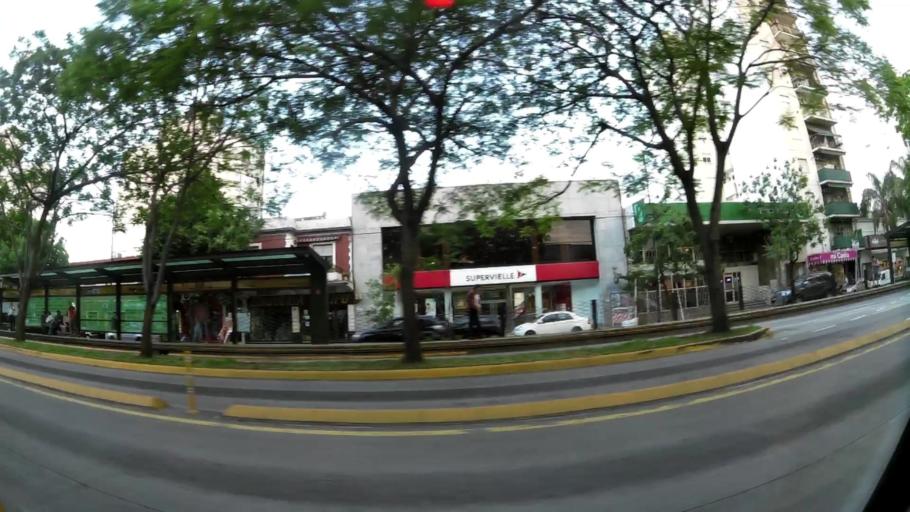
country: AR
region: Buenos Aires
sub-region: Partido de Vicente Lopez
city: Olivos
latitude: -34.5311
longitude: -58.4799
